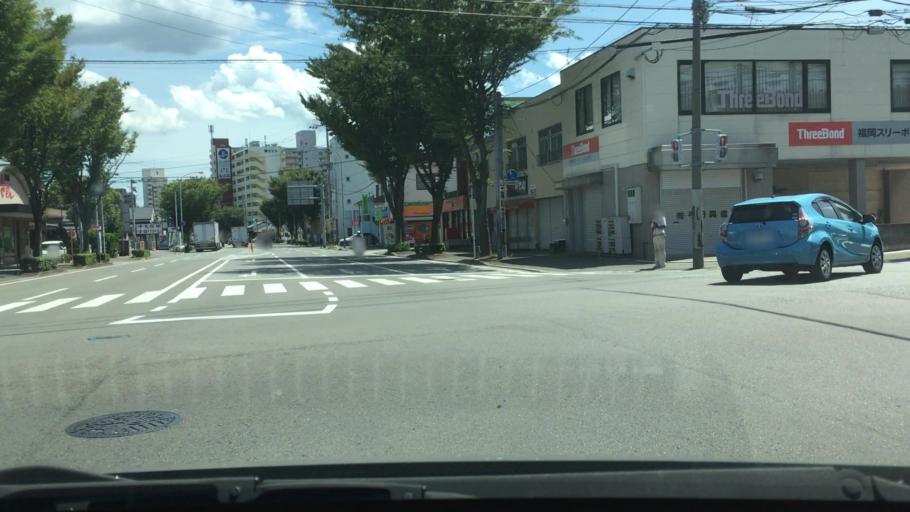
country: JP
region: Fukuoka
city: Onojo
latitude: 33.5643
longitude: 130.4439
